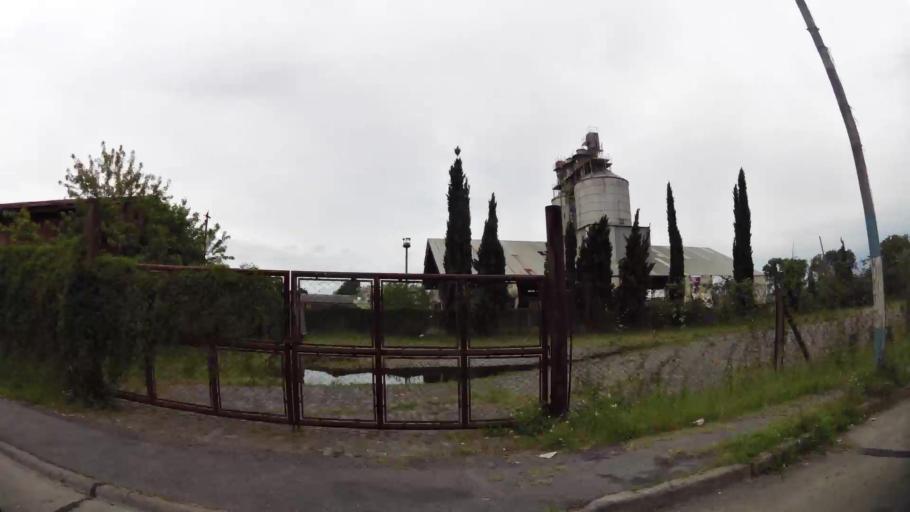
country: AR
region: Buenos Aires
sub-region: Partido de Avellaneda
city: Avellaneda
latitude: -34.6693
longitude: -58.3684
